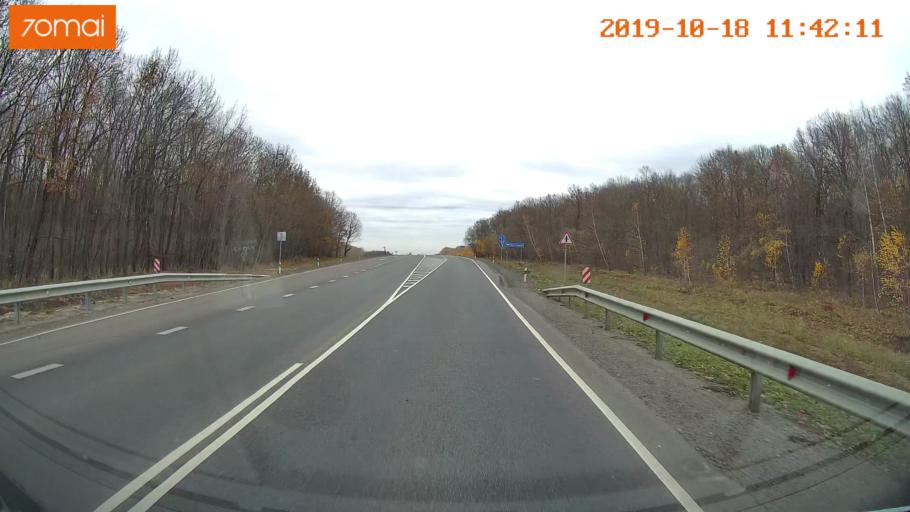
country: RU
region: Rjazan
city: Oktyabr'skiy
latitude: 54.1856
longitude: 38.9225
